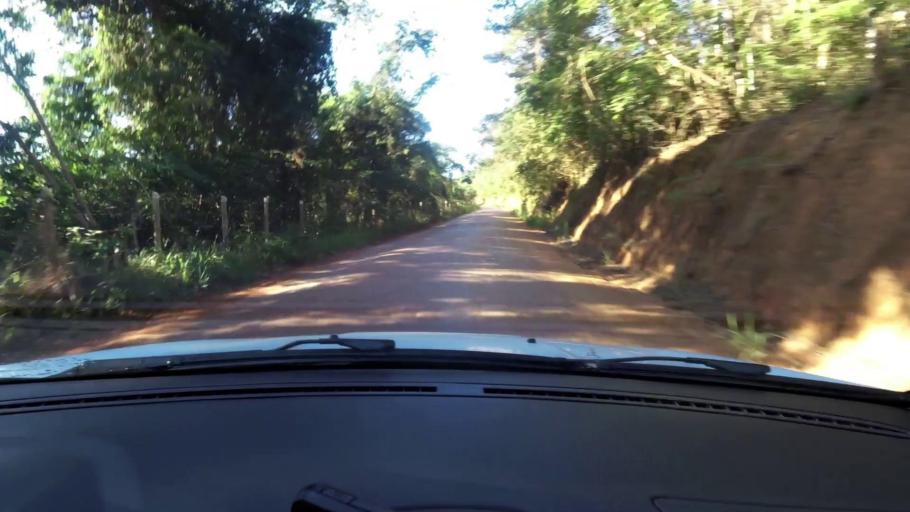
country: BR
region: Espirito Santo
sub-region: Guarapari
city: Guarapari
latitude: -20.7278
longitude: -40.5900
